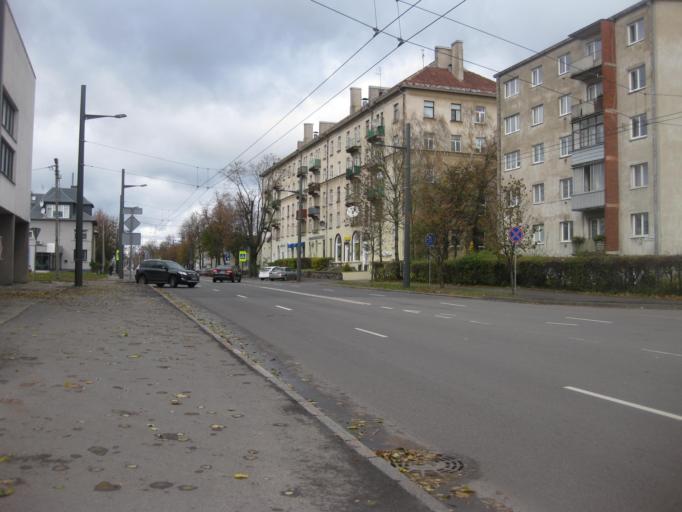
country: LT
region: Kauno apskritis
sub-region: Kaunas
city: Eiguliai
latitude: 54.9061
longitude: 23.9316
